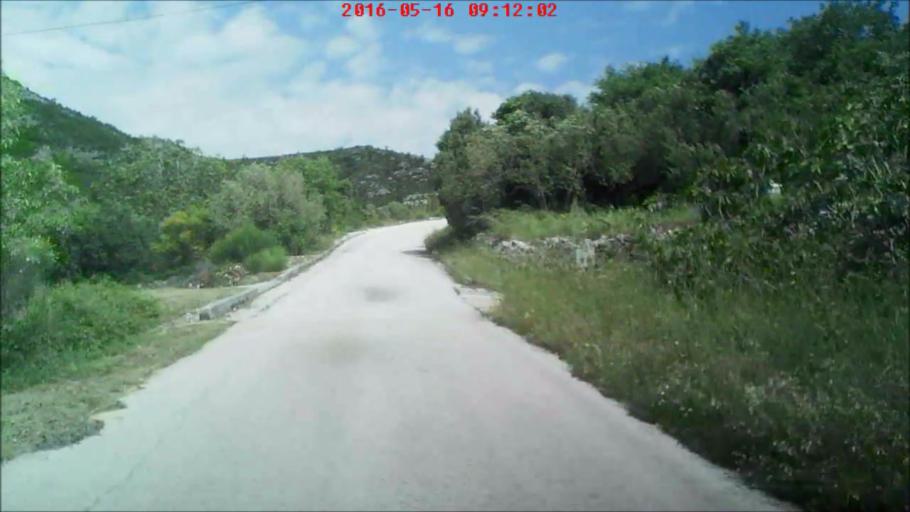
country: HR
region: Dubrovacko-Neretvanska
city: Podgora
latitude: 42.8249
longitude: 17.8509
